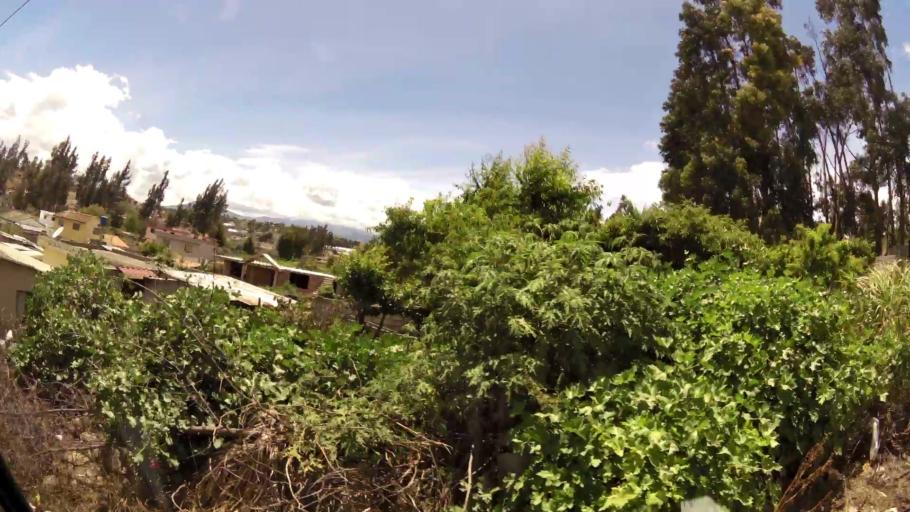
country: EC
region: Tungurahua
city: Ambato
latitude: -1.2839
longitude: -78.6021
